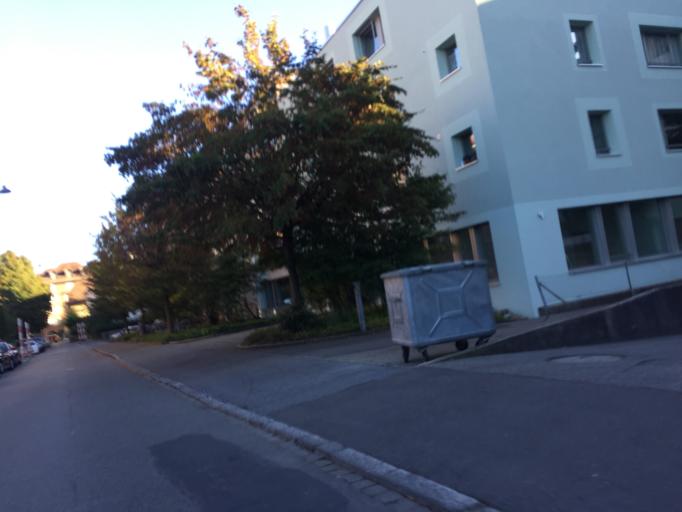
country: CH
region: Bern
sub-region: Bern-Mittelland District
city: Bern
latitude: 46.9418
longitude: 7.4287
